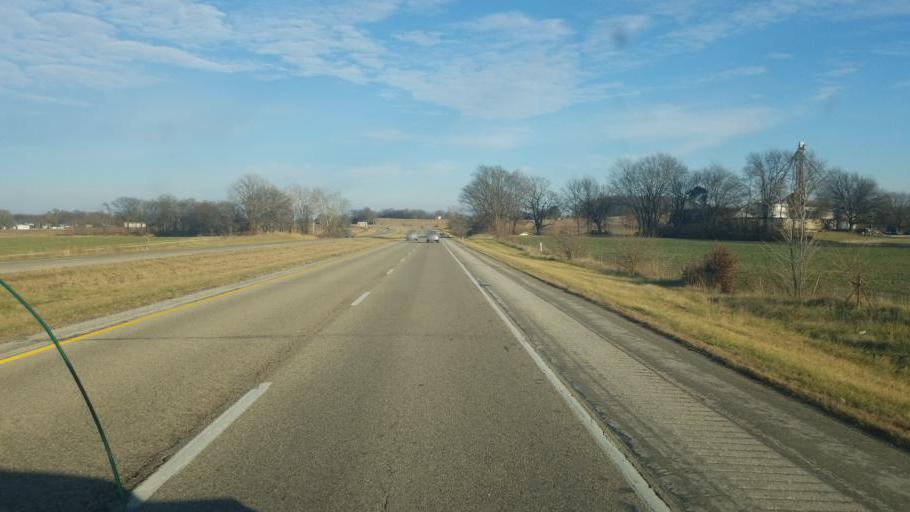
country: US
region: Indiana
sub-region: Knox County
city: Vincennes
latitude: 38.6752
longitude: -87.4337
